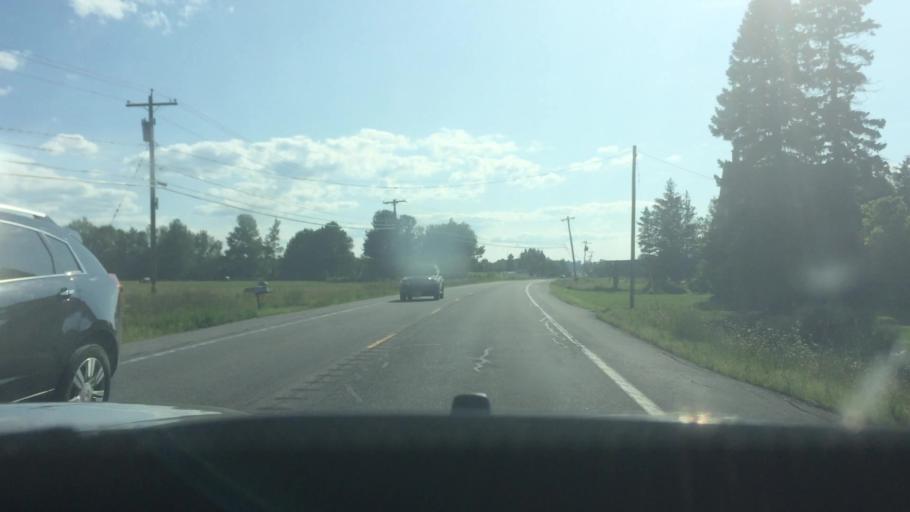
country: US
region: New York
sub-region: Franklin County
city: Malone
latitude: 44.8316
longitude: -74.3300
